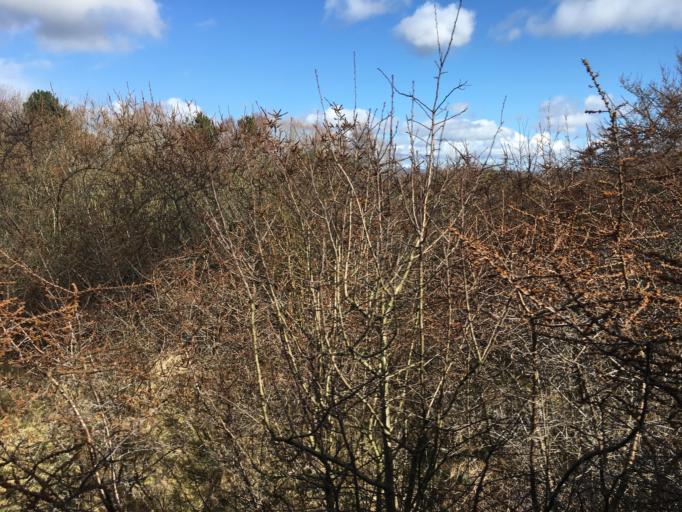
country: GB
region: Scotland
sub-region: Falkirk
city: Bo'ness
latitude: 56.0154
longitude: -3.6185
